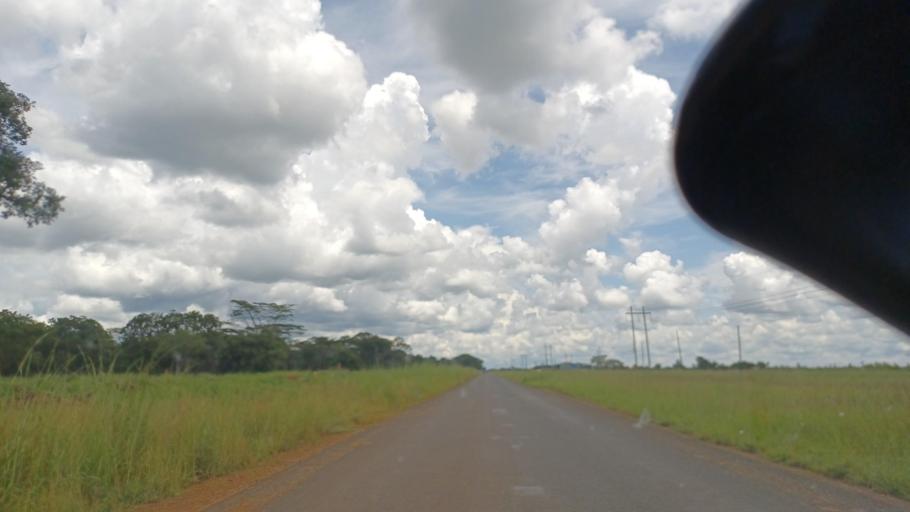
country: ZM
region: North-Western
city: Solwezi
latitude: -12.4413
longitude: 26.2088
